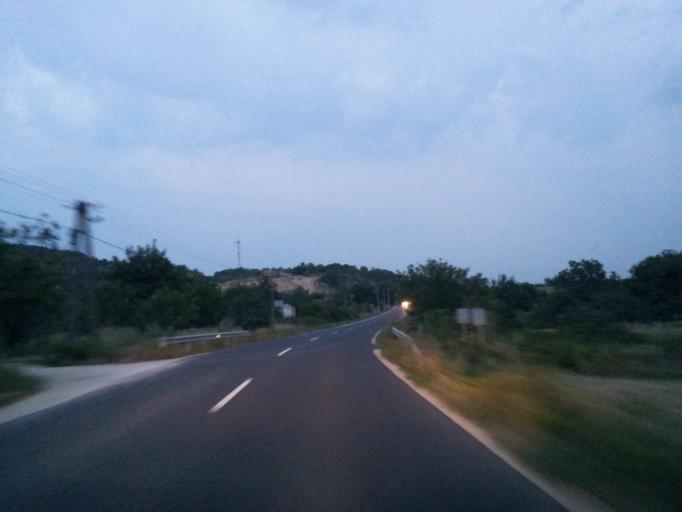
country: HU
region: Veszprem
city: Sumeg
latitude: 46.9764
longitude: 17.2971
